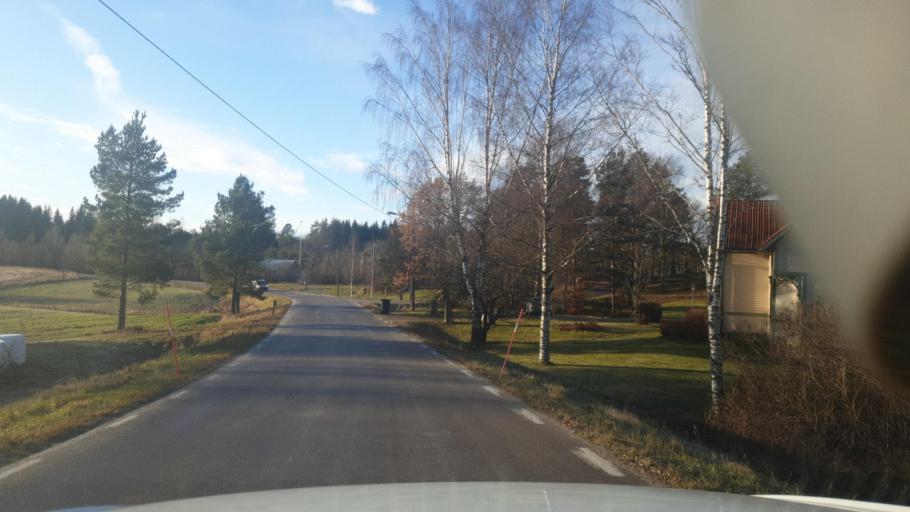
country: SE
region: Vaermland
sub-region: Karlstads Kommun
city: Edsvalla
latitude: 59.5687
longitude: 13.0564
